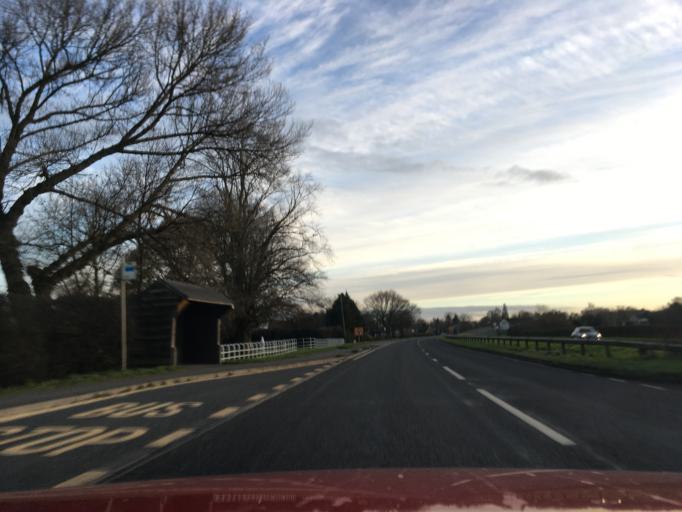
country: GB
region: England
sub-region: Staffordshire
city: Stone
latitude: 52.8791
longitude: -2.1323
